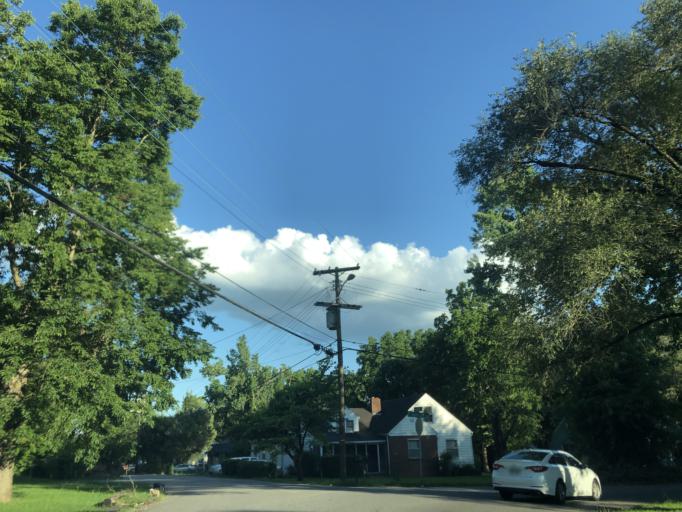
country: US
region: Tennessee
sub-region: Davidson County
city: Nashville
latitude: 36.1903
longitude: -86.8348
